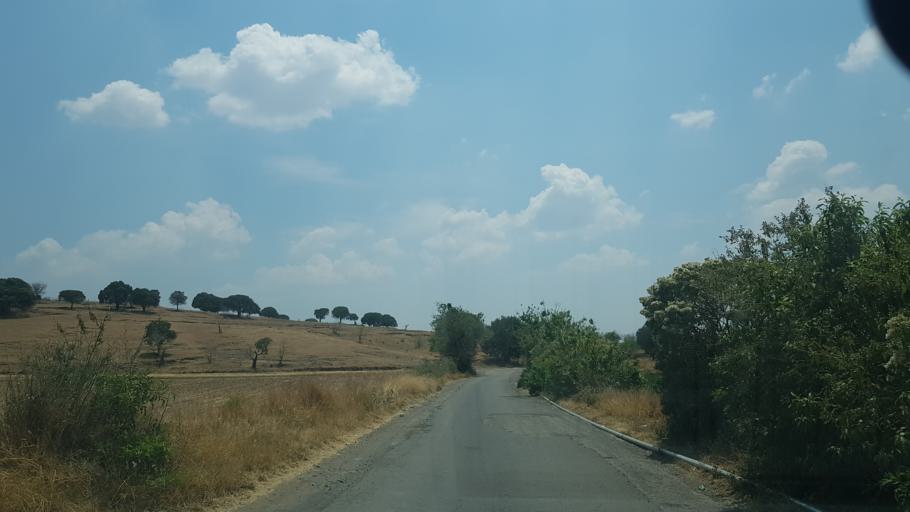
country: MX
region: Puebla
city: San Juan Amecac
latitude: 18.8319
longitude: -98.6204
